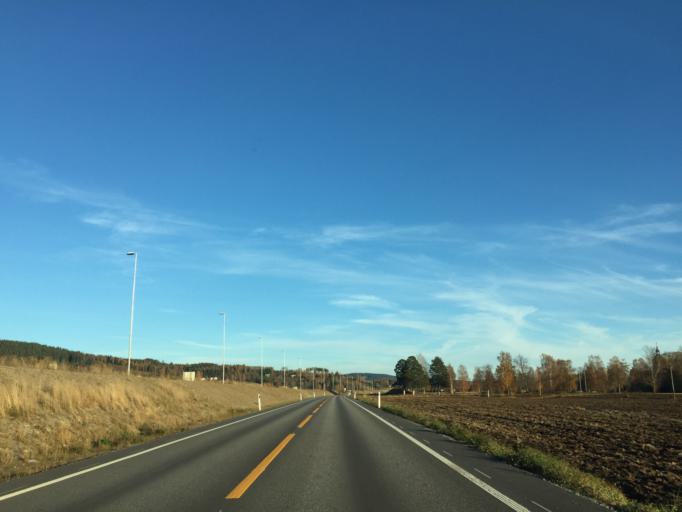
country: NO
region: Hedmark
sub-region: Sor-Odal
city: Skarnes
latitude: 60.2460
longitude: 11.7562
